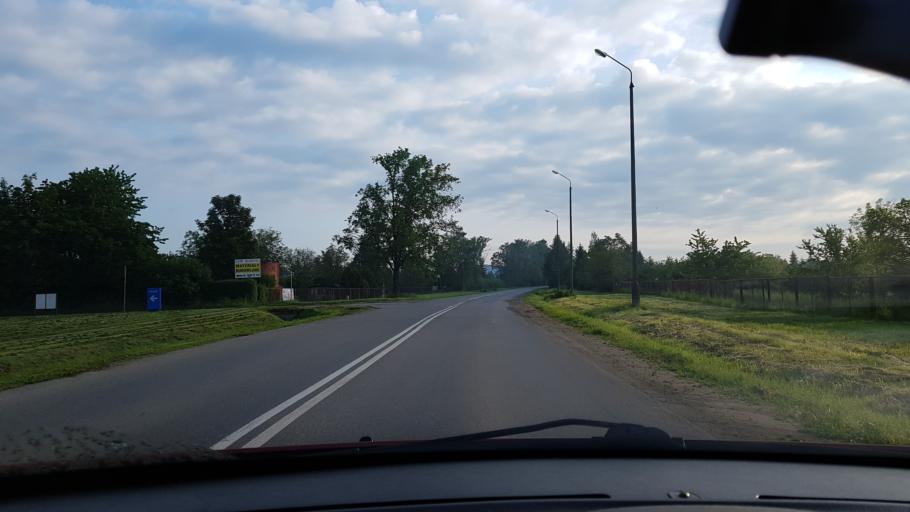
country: PL
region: Lower Silesian Voivodeship
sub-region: Powiat zabkowicki
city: Zabkowice Slaskie
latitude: 50.6026
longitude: 16.8201
